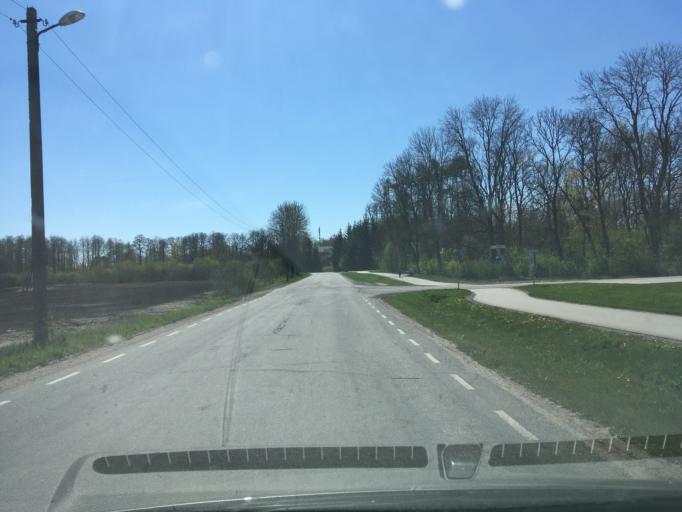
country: EE
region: Harju
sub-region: Raasiku vald
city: Arukula
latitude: 59.3624
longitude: 25.0825
